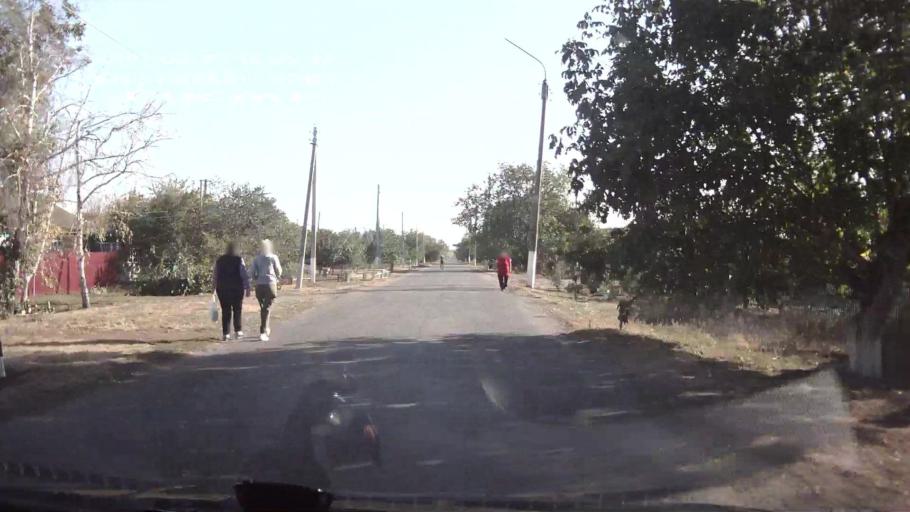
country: RU
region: Rostov
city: Gigant
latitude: 46.5252
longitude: 41.1902
